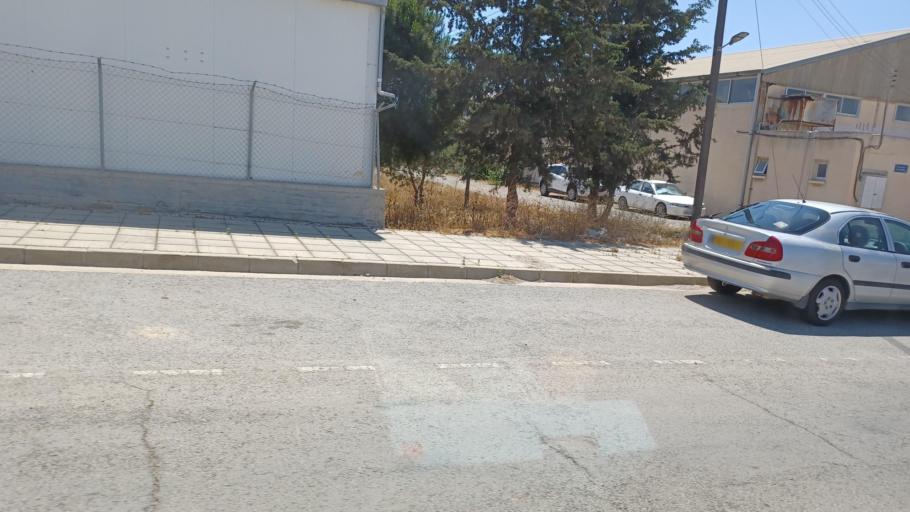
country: CY
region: Ammochostos
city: Frenaros
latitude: 35.0342
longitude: 33.9132
